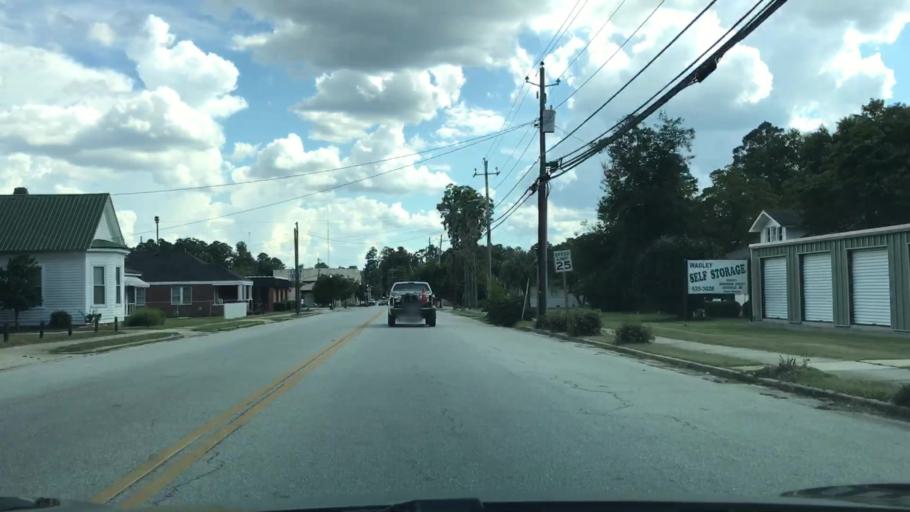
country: US
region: Georgia
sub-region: Jefferson County
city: Wadley
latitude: 32.8645
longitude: -82.4047
